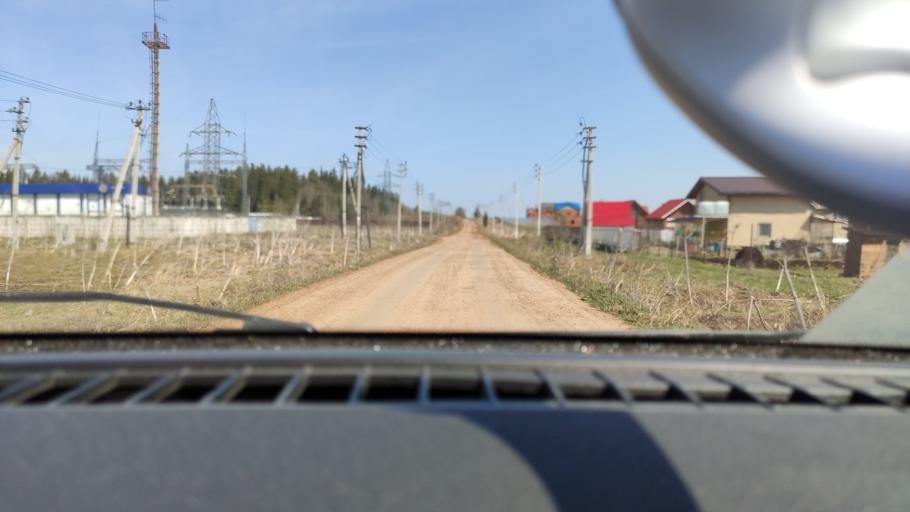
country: RU
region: Perm
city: Kultayevo
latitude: 57.8809
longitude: 55.8455
